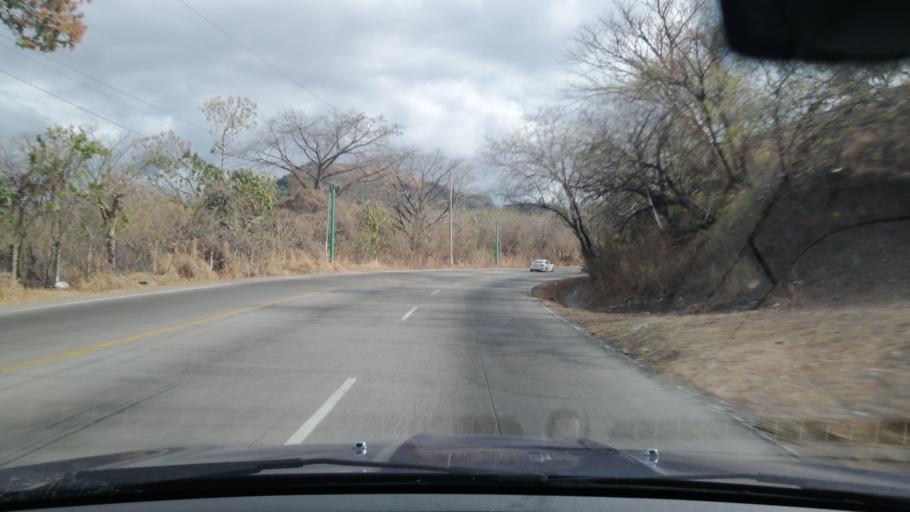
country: SV
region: Santa Ana
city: Texistepeque
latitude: 14.0612
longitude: -89.5085
